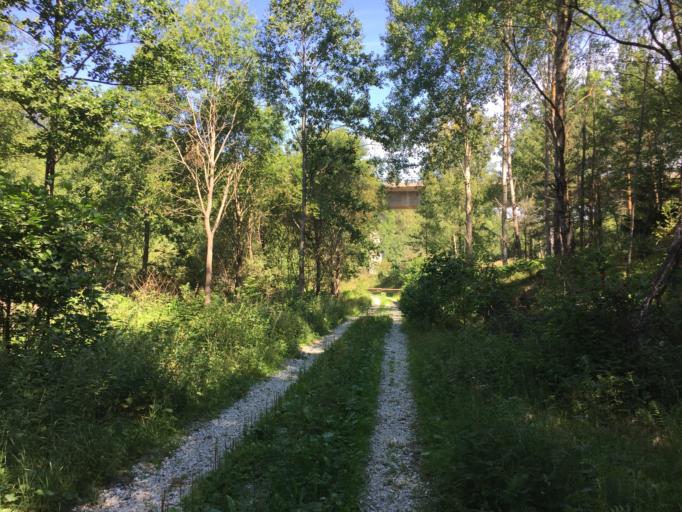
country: SE
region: Stockholm
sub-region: Botkyrka Kommun
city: Varsta
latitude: 59.1500
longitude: 17.7980
